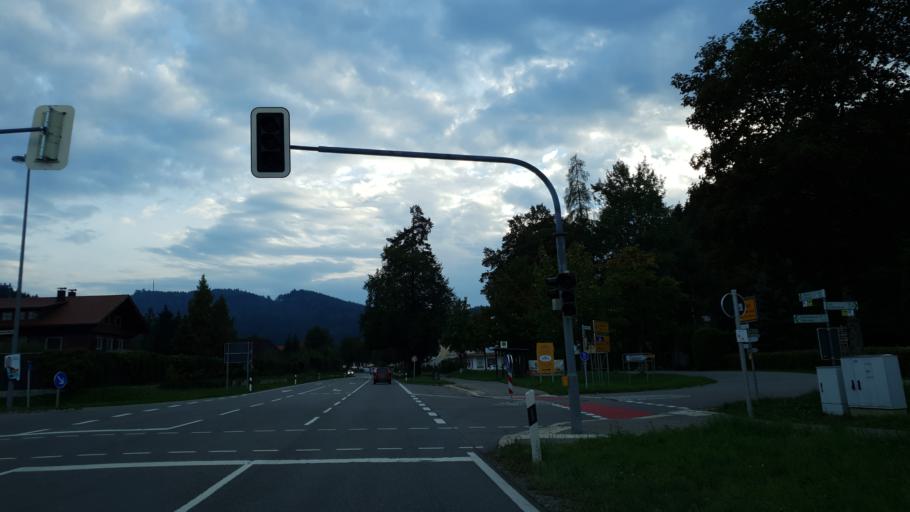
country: DE
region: Bavaria
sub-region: Swabia
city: Weitnau
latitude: 47.6611
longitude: 10.0929
